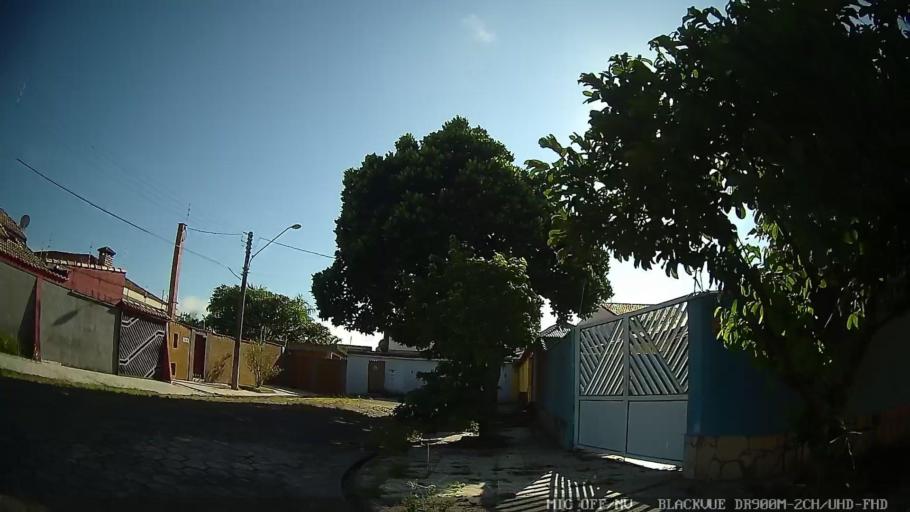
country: BR
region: Sao Paulo
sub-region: Peruibe
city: Peruibe
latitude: -24.2799
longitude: -46.9454
